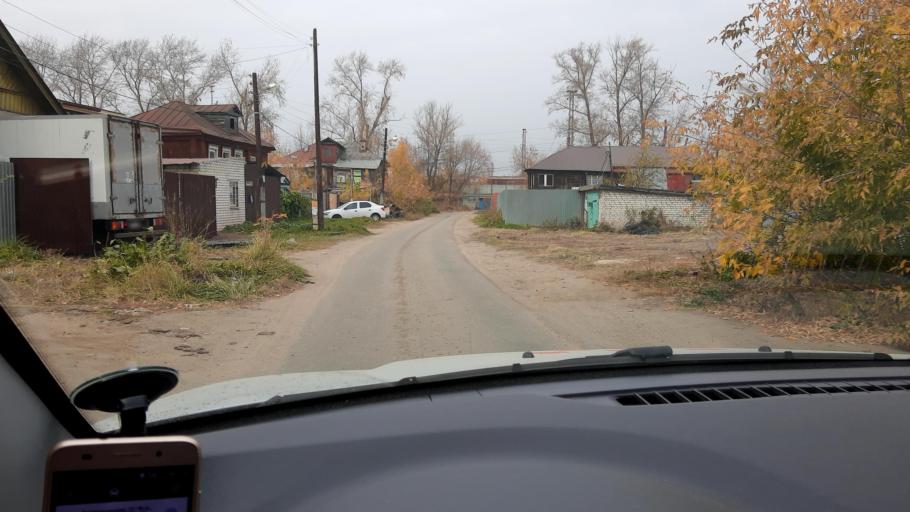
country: RU
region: Nizjnij Novgorod
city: Nizhniy Novgorod
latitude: 56.3120
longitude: 43.9247
